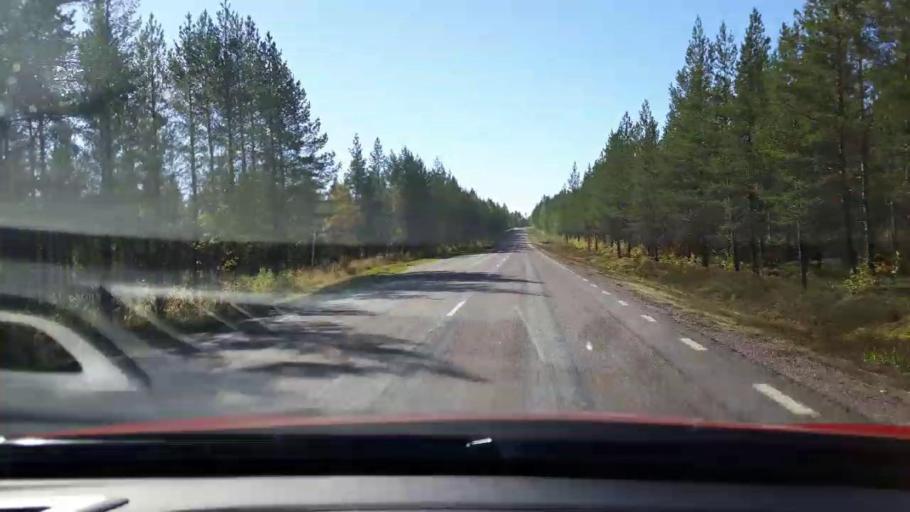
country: SE
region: Jaemtland
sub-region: Harjedalens Kommun
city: Sveg
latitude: 62.1342
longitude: 14.1687
